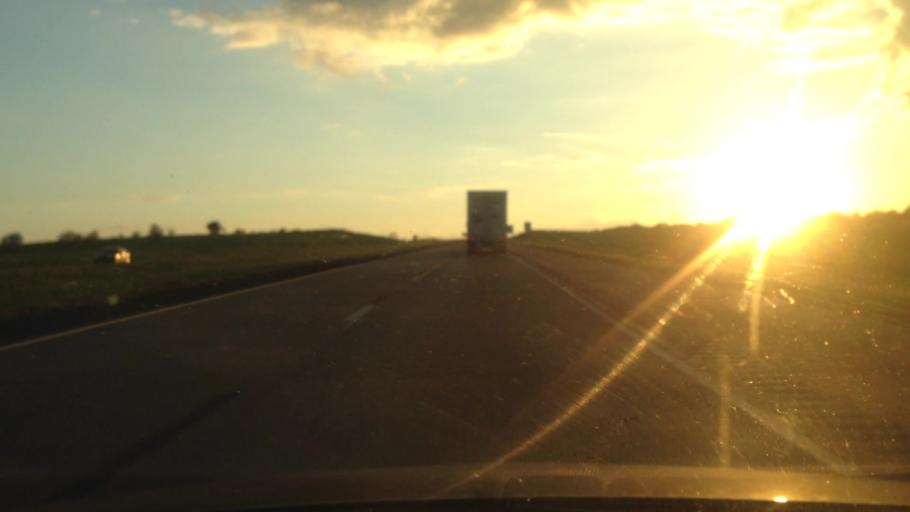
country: US
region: Texas
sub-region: Tarrant County
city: Benbrook
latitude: 32.6946
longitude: -97.4888
